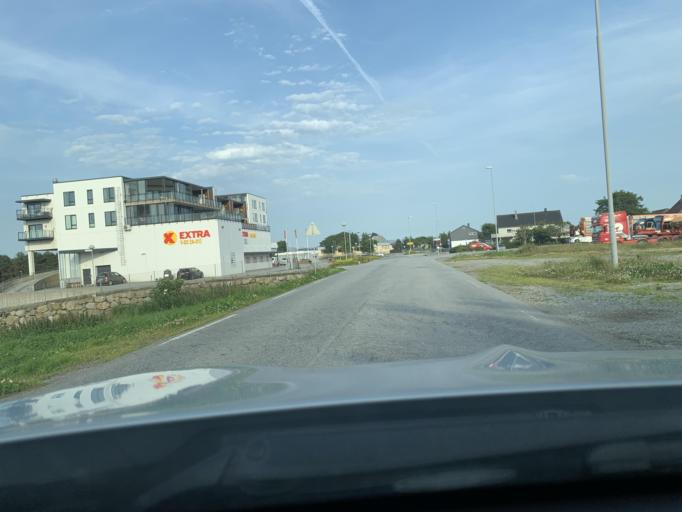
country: NO
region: Rogaland
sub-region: Time
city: Bryne
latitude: 58.7186
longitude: 5.5663
